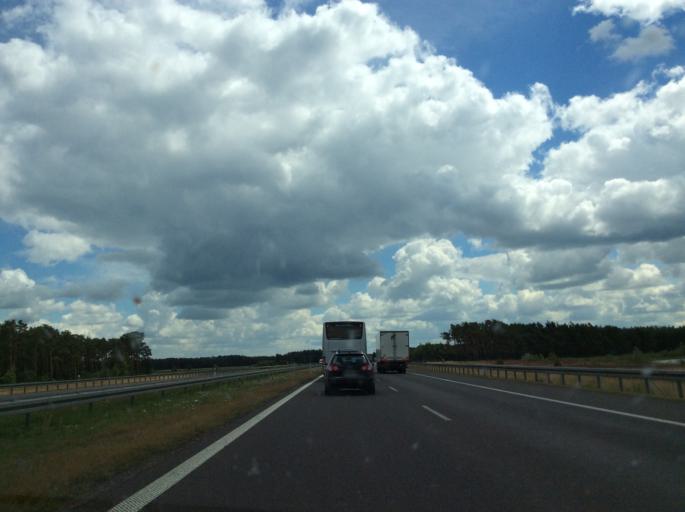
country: PL
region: Greater Poland Voivodeship
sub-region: Powiat kolski
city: Dabie
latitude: 52.0883
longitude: 18.7888
